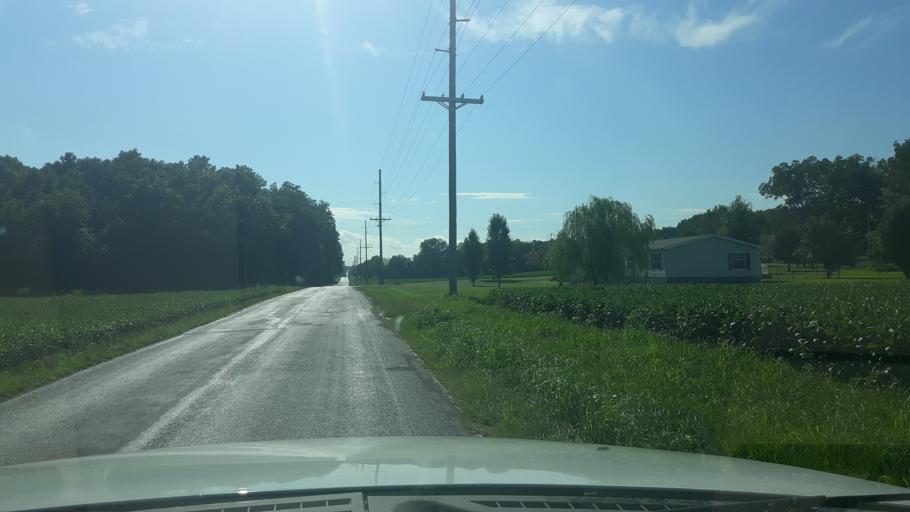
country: US
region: Illinois
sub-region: Saline County
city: Harrisburg
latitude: 37.8630
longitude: -88.5578
